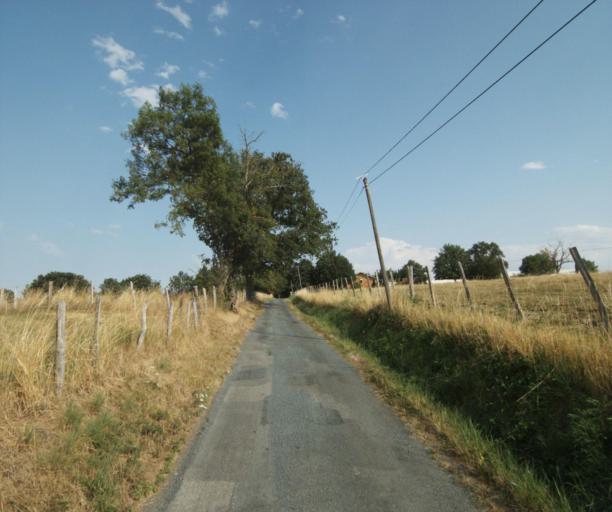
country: FR
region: Rhone-Alpes
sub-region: Departement du Rhone
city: Savigny
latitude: 45.8235
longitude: 4.5857
